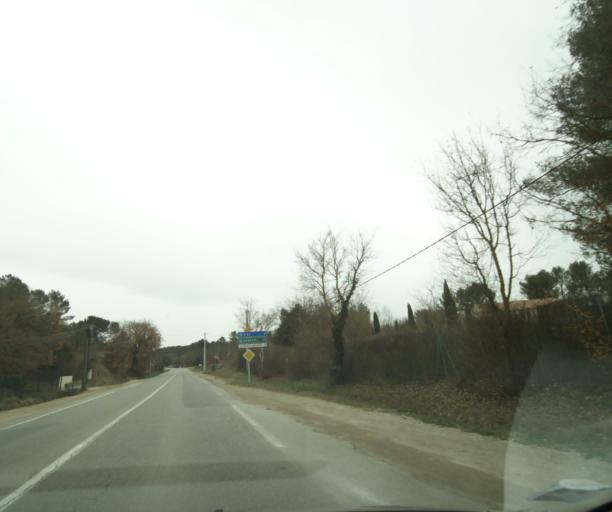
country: FR
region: Provence-Alpes-Cote d'Azur
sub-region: Departement des Bouches-du-Rhone
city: Greasque
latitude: 43.4426
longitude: 5.5536
